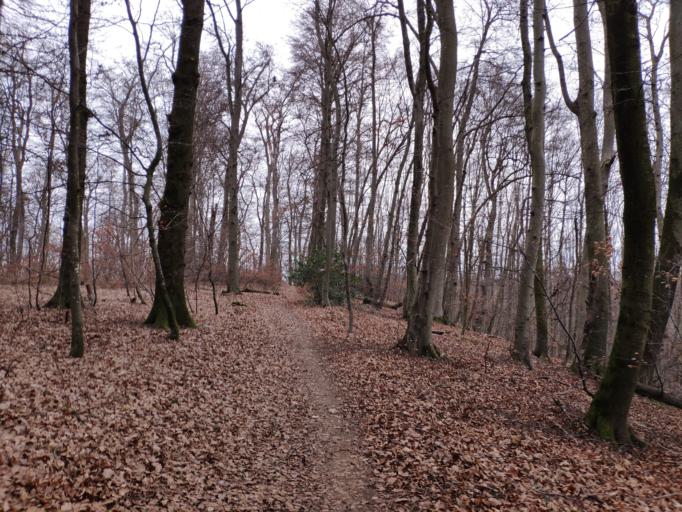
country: DE
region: Baden-Wuerttemberg
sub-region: Freiburg Region
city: Inzlingen
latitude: 47.5820
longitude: 7.6811
